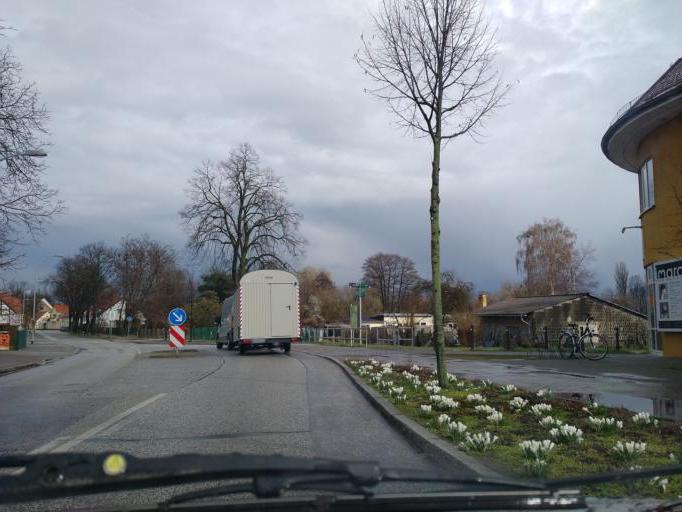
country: DE
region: Brandenburg
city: Falkensee
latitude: 52.5640
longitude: 13.0984
